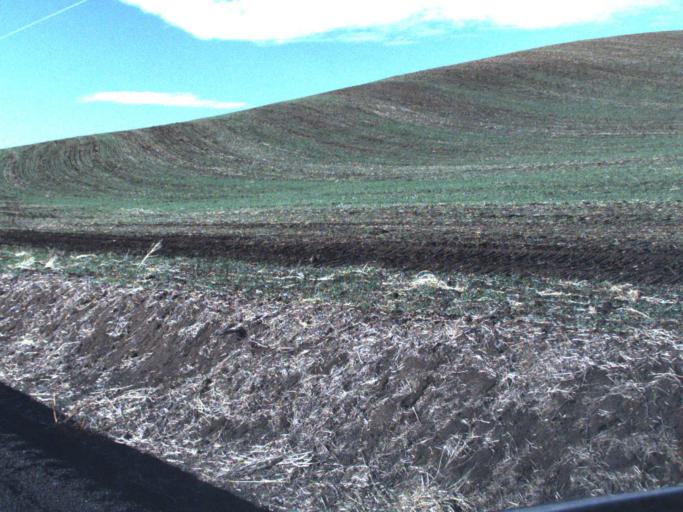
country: US
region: Washington
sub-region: Whitman County
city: Pullman
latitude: 46.7189
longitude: -117.2550
